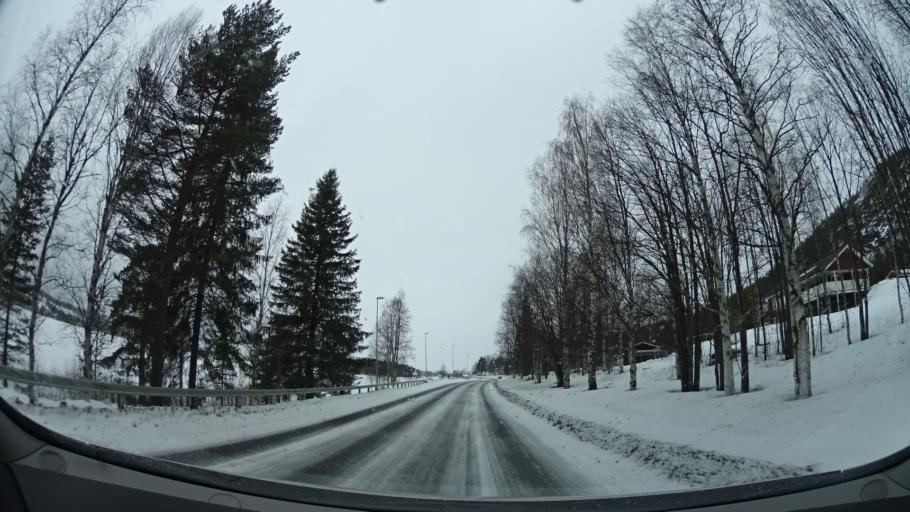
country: SE
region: Vaesterbotten
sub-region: Mala Kommun
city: Mala
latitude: 65.1736
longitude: 18.7577
